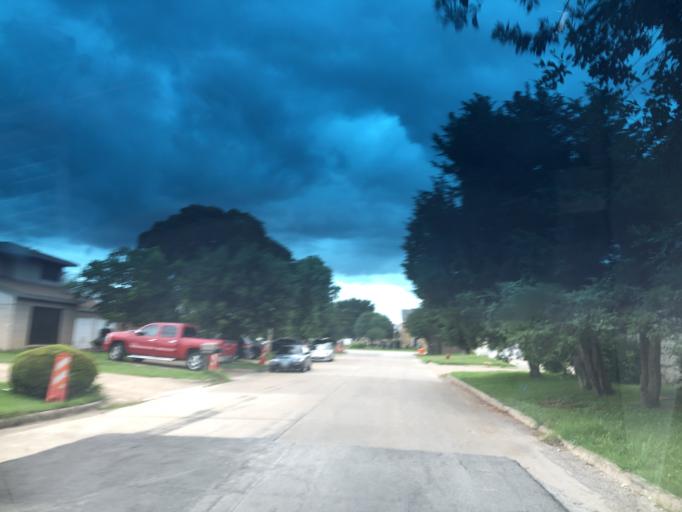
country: US
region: Texas
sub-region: Dallas County
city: Grand Prairie
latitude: 32.6972
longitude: -97.0128
